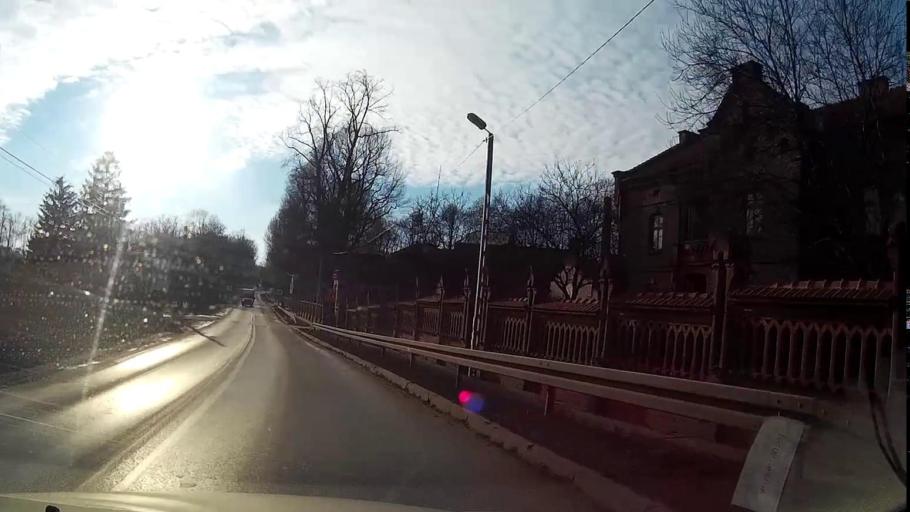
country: PL
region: Lesser Poland Voivodeship
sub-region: Powiat krakowski
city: Kryspinow
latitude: 50.0426
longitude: 19.8425
